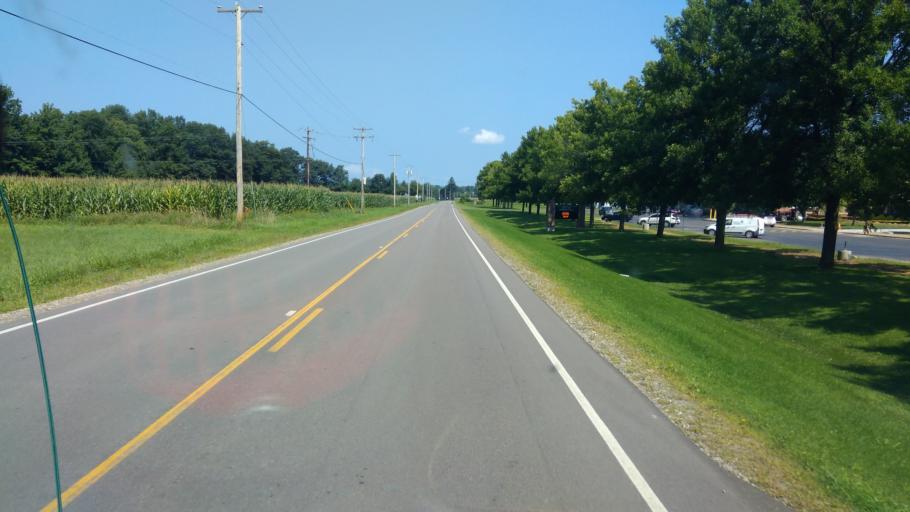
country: US
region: New York
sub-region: Allegany County
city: Belmont
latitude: 42.2393
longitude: -78.0406
